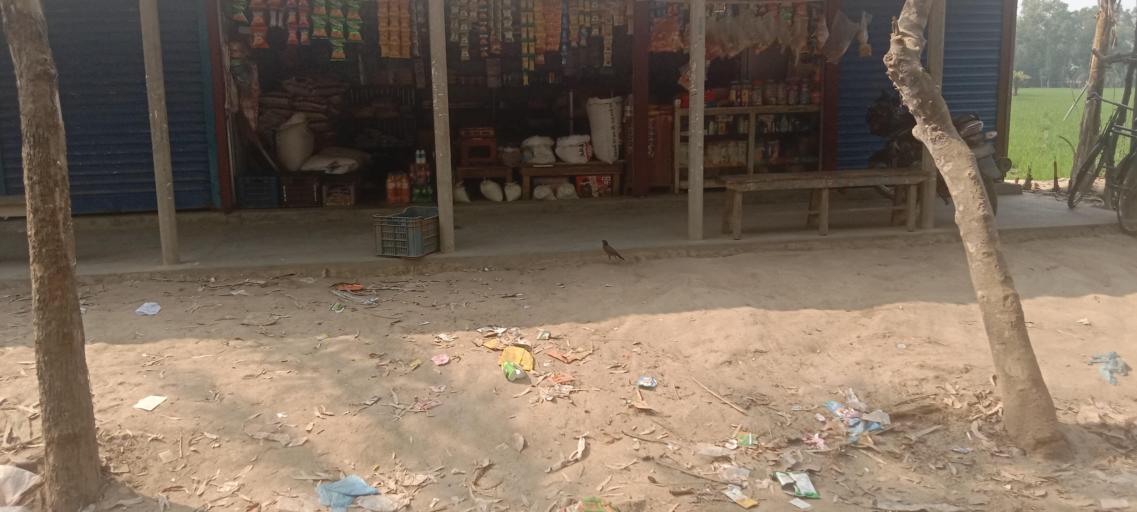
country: BD
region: Dhaka
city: Sakhipur
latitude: 24.3355
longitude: 90.2881
